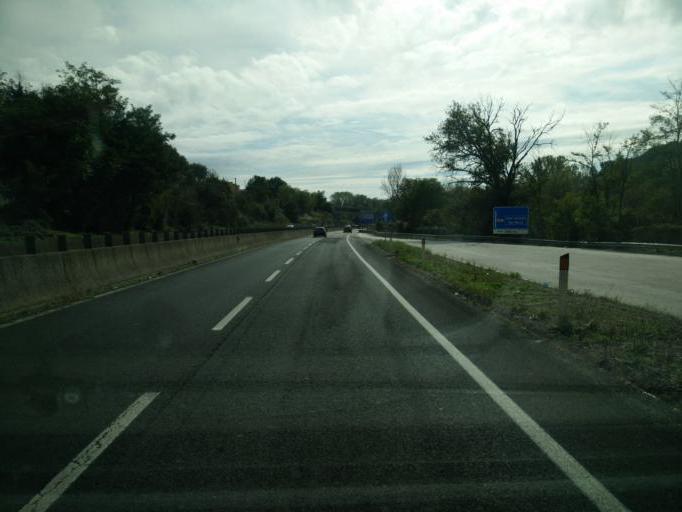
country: IT
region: Tuscany
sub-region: Provincia di Siena
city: Siena
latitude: 43.3129
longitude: 11.3098
